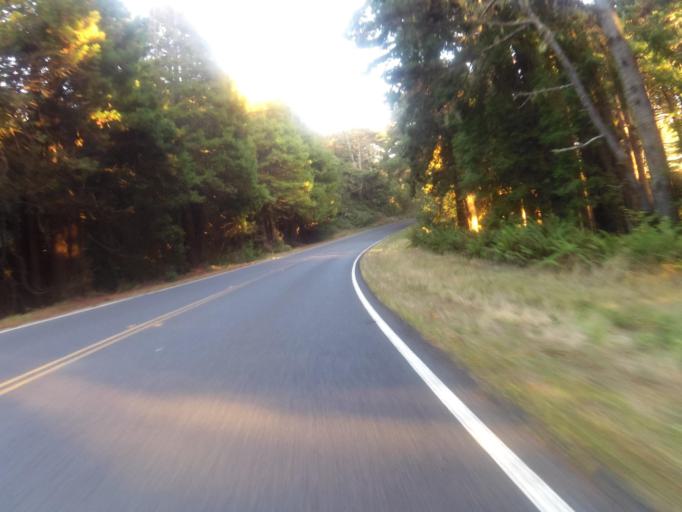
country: US
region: California
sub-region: Sonoma County
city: Sea Ranch
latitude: 38.6511
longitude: -123.3984
